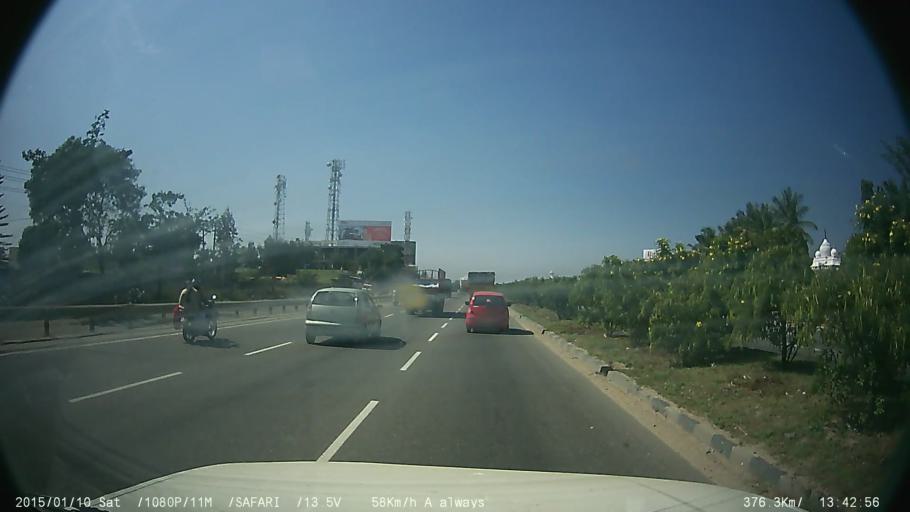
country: IN
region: Karnataka
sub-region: Bangalore Urban
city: Anekal
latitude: 12.7874
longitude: 77.7384
